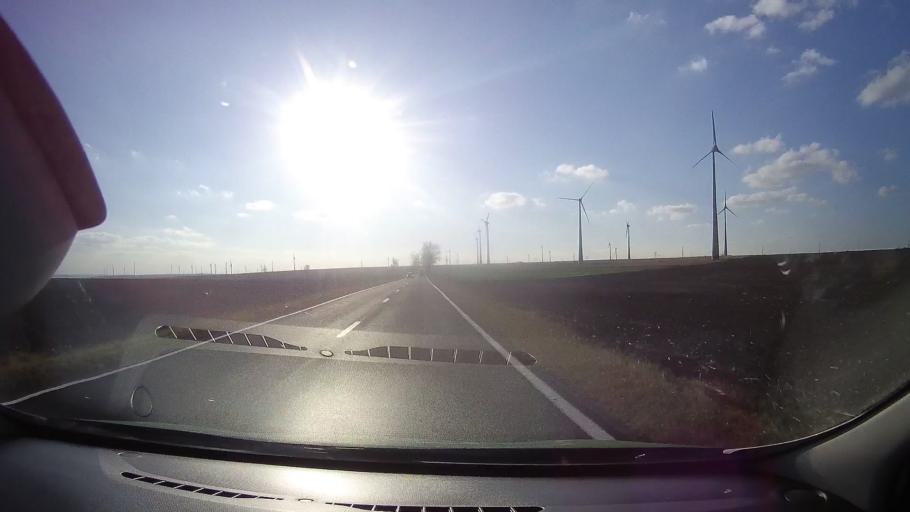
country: RO
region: Tulcea
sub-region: Comuna Topolog
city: Topolog
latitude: 44.8289
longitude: 28.2803
